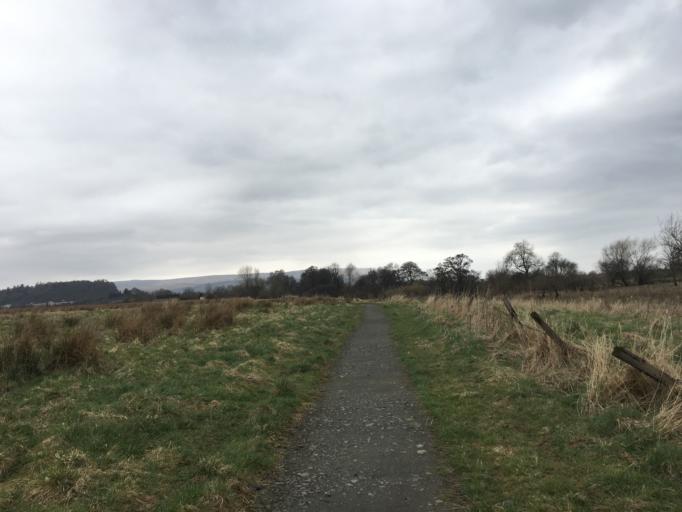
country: GB
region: Scotland
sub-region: Stirling
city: Bridge of Allan
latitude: 56.1417
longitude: -3.9597
